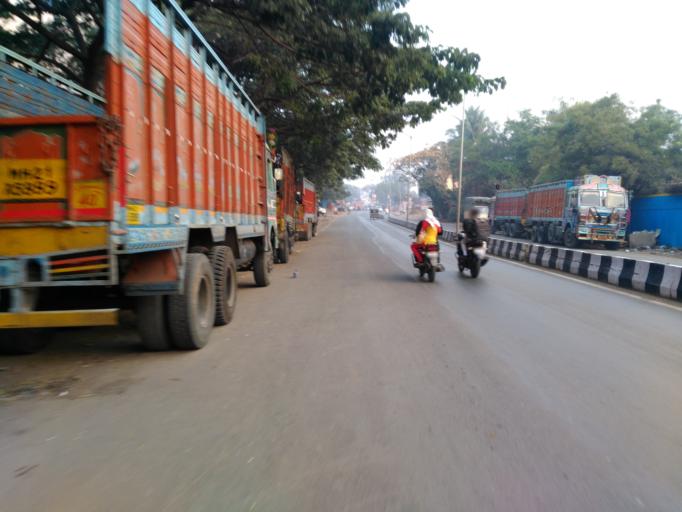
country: IN
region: Maharashtra
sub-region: Pune Division
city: Pune
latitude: 18.4555
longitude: 73.8906
